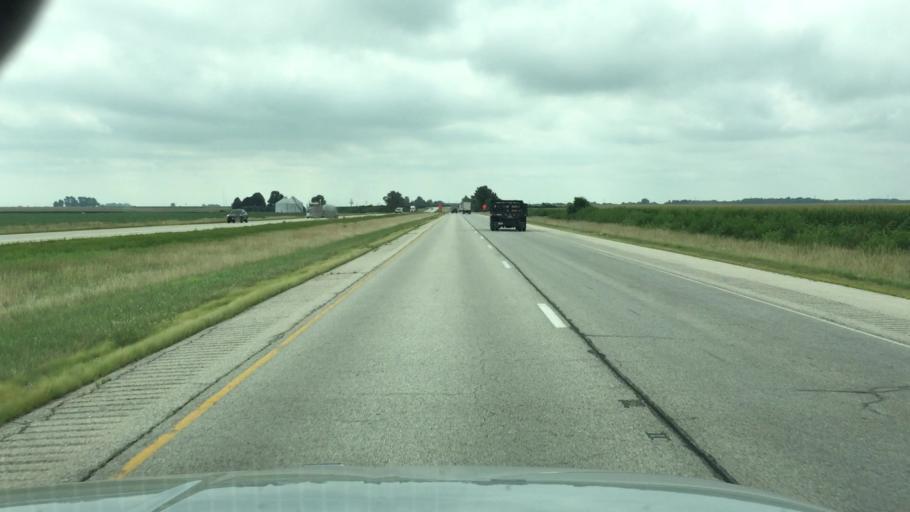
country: US
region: Illinois
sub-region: Knox County
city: Galesburg
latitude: 41.0417
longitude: -90.3345
